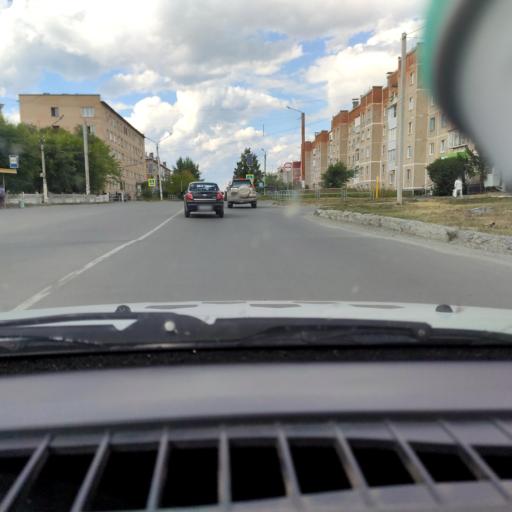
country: RU
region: Chelyabinsk
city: Miass
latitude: 55.0783
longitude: 60.0935
